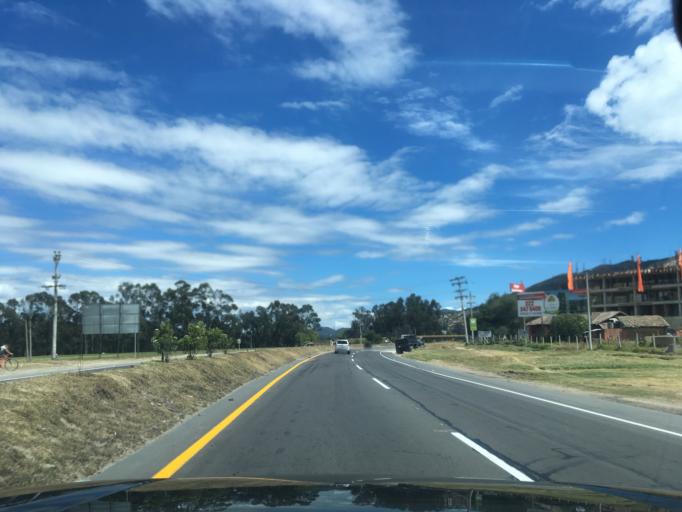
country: CO
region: Cundinamarca
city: Tocancipa
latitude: 4.9672
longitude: -73.9047
